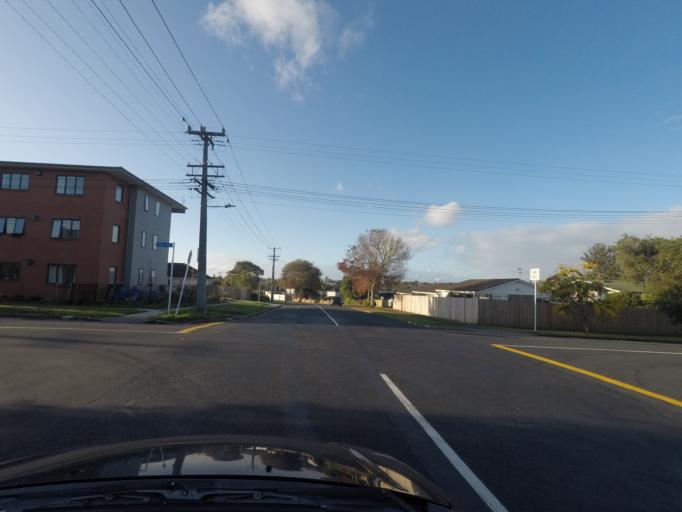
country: NZ
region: Auckland
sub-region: Auckland
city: Waitakere
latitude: -36.9050
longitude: 174.6763
